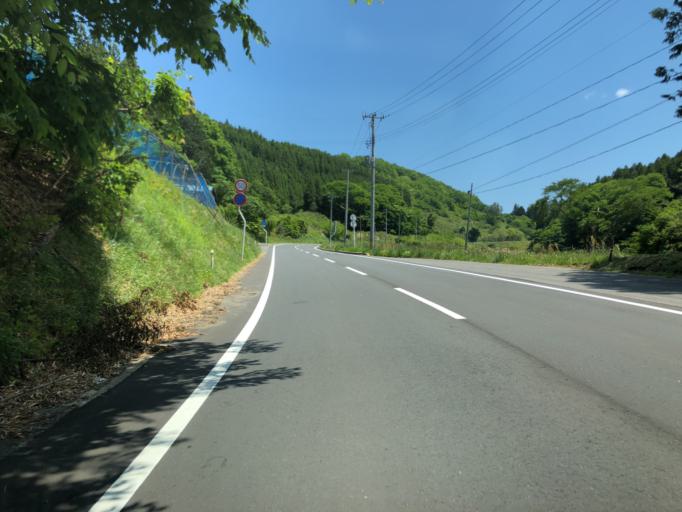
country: JP
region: Fukushima
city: Funehikimachi-funehiki
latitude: 37.5136
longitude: 140.6709
